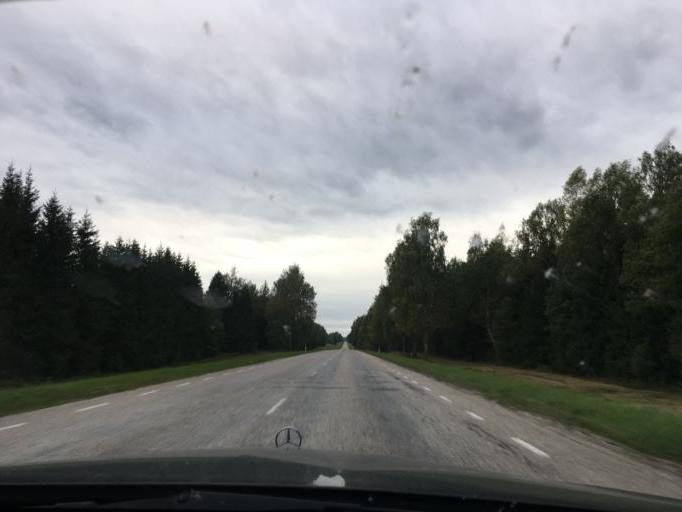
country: LV
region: Aluksnes Rajons
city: Aluksne
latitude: 57.5975
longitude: 27.2035
